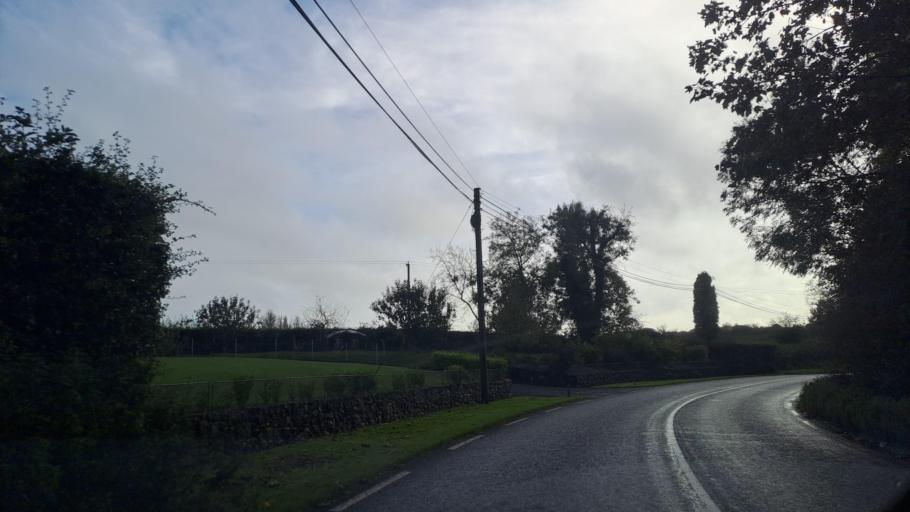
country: IE
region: Ulster
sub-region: County Monaghan
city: Carrickmacross
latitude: 53.9447
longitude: -6.7159
